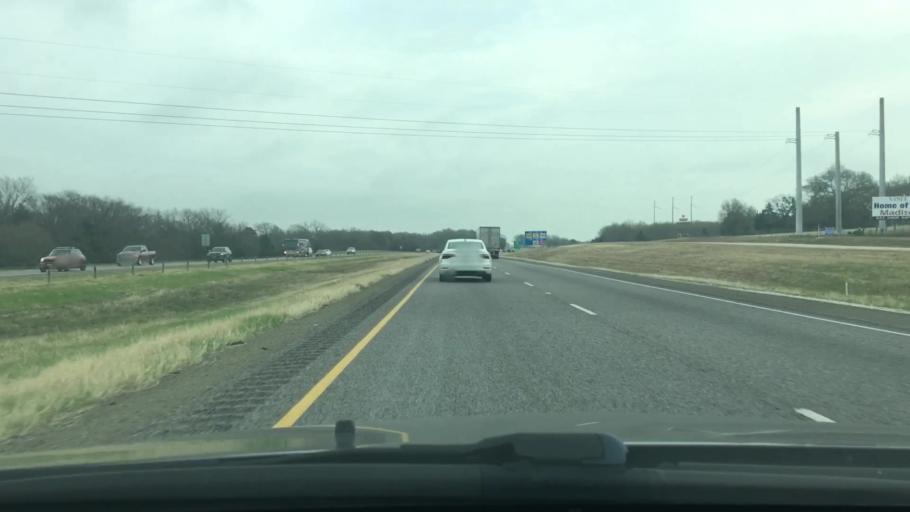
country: US
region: Texas
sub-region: Freestone County
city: Fairfield
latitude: 31.7357
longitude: -96.1859
